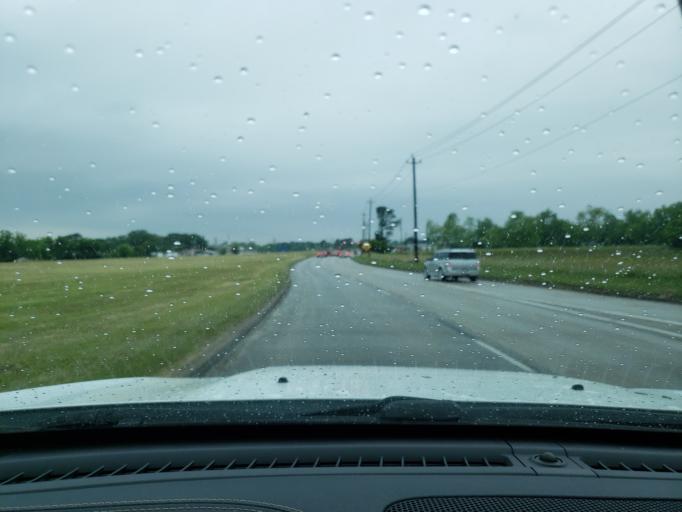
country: US
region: Texas
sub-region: Harris County
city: Baytown
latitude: 29.7607
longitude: -94.9251
